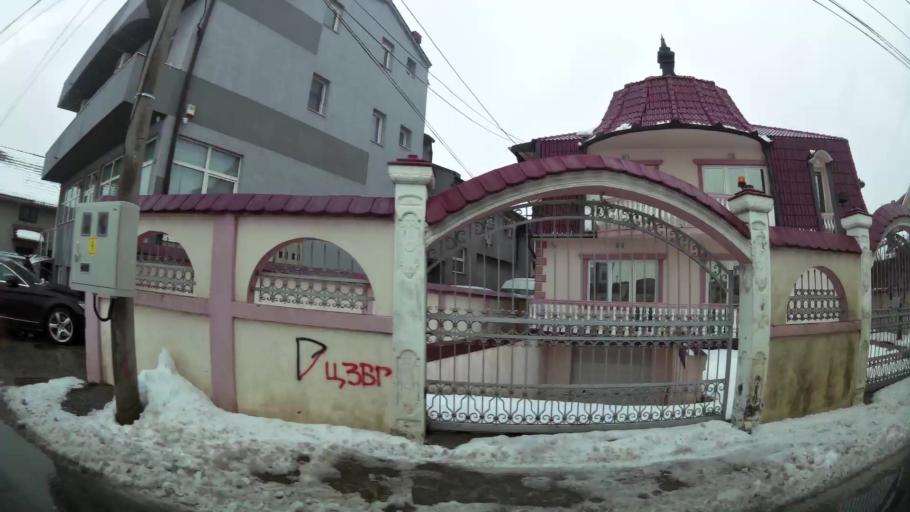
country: RS
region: Central Serbia
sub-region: Belgrade
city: Zemun
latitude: 44.8470
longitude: 20.3617
